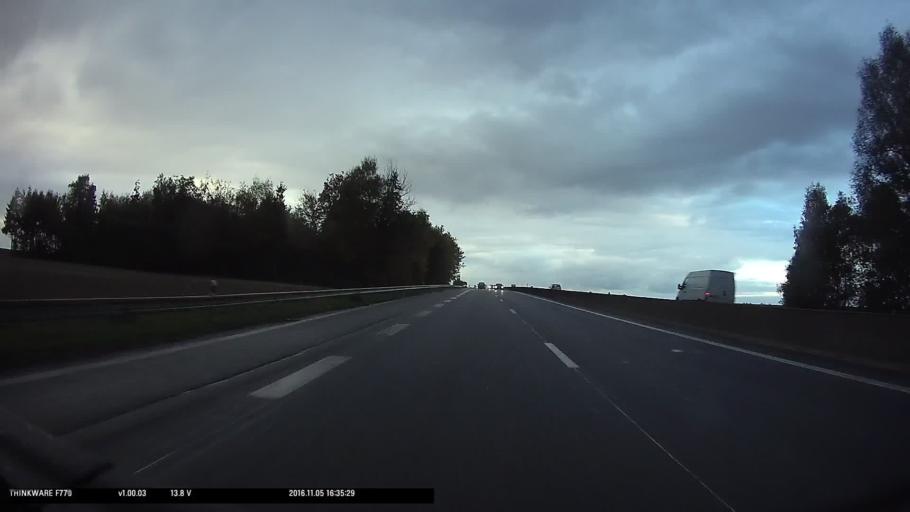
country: FR
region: Ile-de-France
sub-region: Departement du Val-d'Oise
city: Ableiges
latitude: 49.0640
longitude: 1.9820
